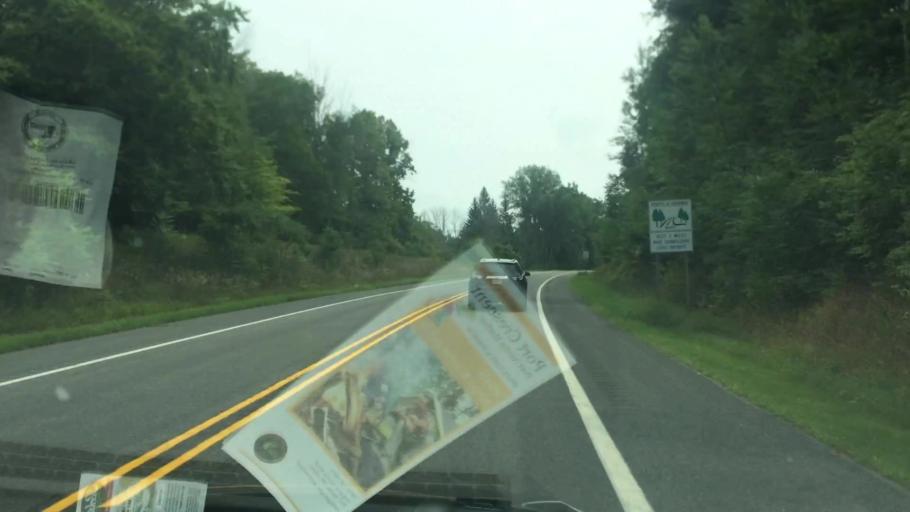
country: US
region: Michigan
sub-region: Huron County
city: Harbor Beach
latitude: 44.0199
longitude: -82.8077
